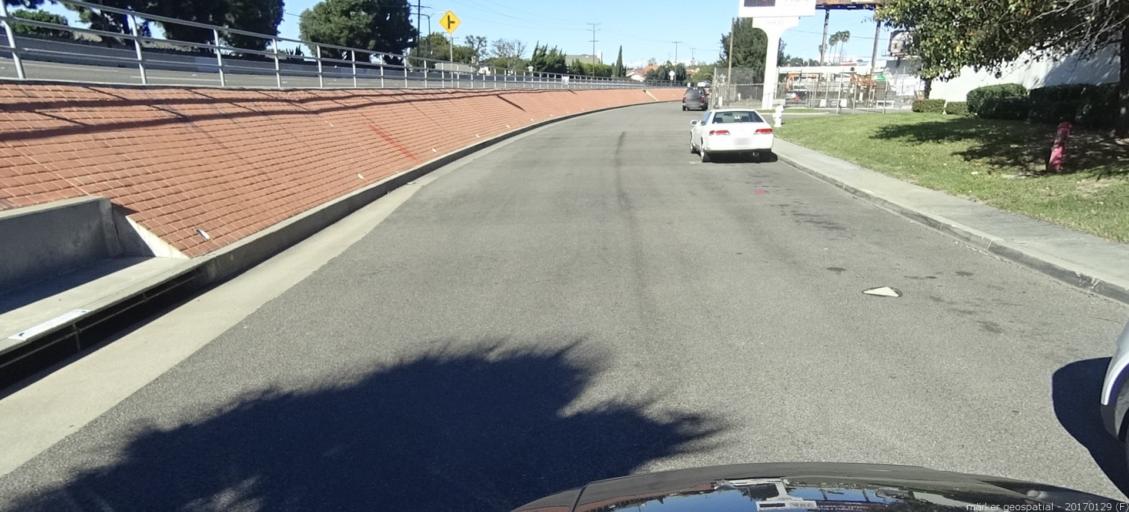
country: US
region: California
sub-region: Orange County
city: Fountain Valley
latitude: 33.7186
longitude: -117.9209
